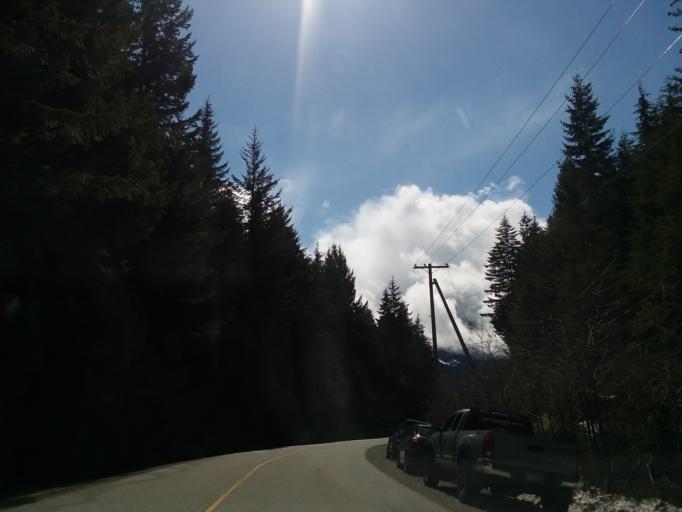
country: CA
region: British Columbia
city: Whistler
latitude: 50.1238
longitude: -122.9864
